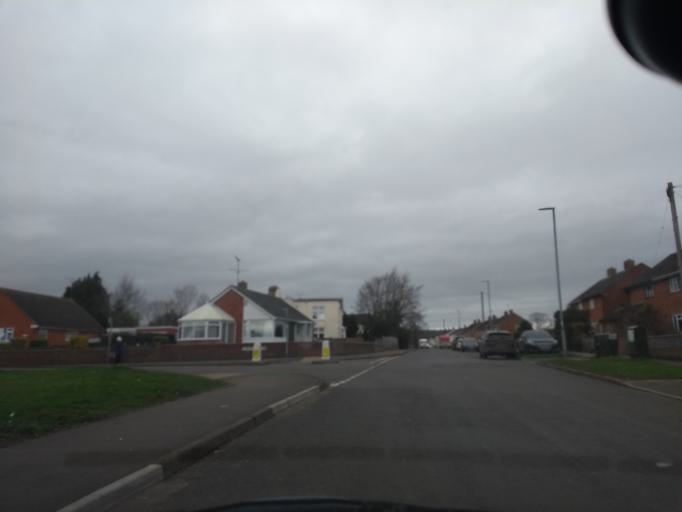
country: GB
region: England
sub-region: Somerset
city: Taunton
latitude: 51.0354
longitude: -3.1016
